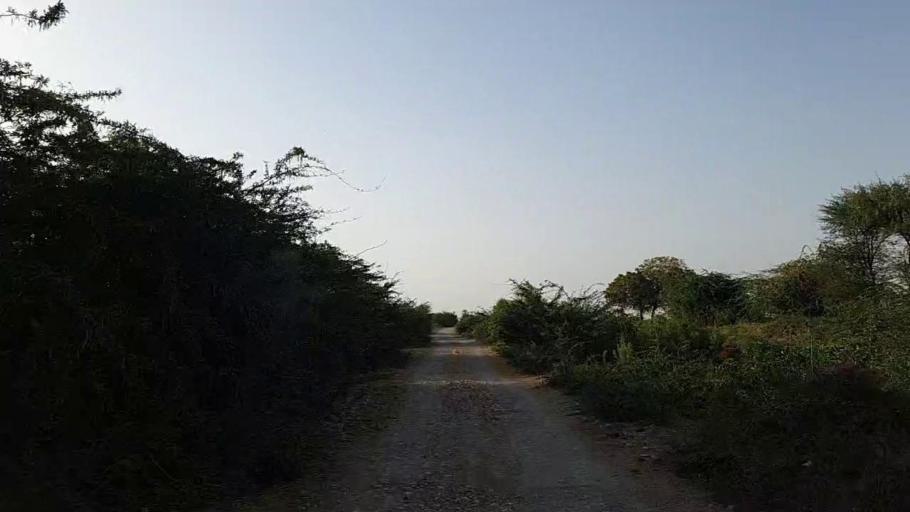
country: PK
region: Sindh
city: Jati
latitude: 24.3415
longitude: 68.1475
